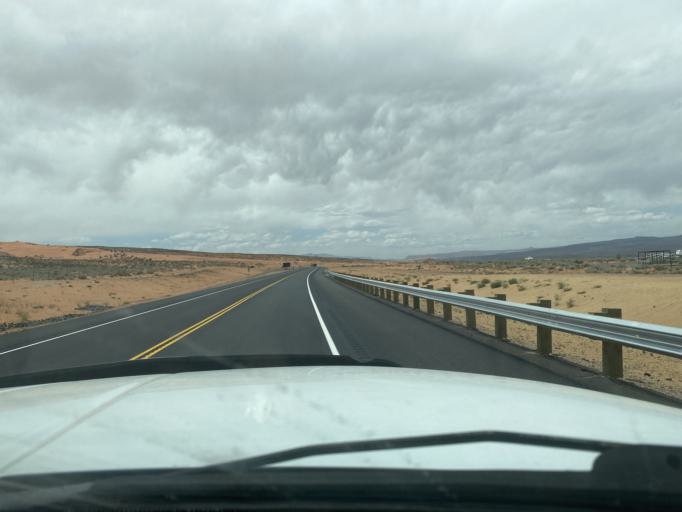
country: US
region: Utah
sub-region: Washington County
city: Hurricane
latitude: 37.0982
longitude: -113.3675
